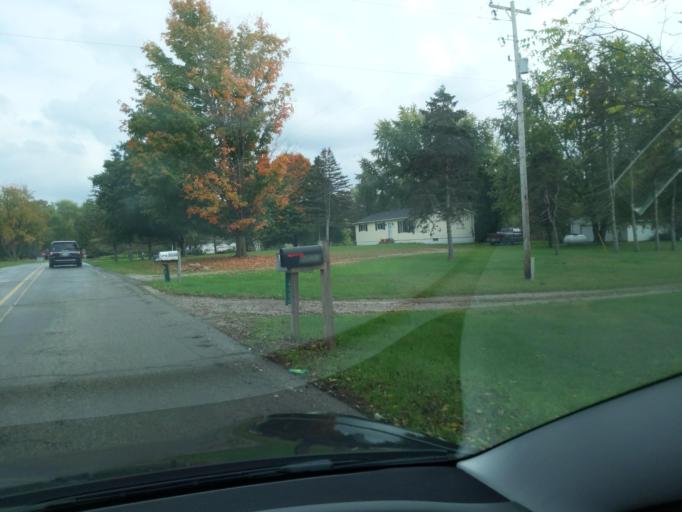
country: US
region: Michigan
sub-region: Ingham County
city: Leslie
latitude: 42.4121
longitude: -84.3770
